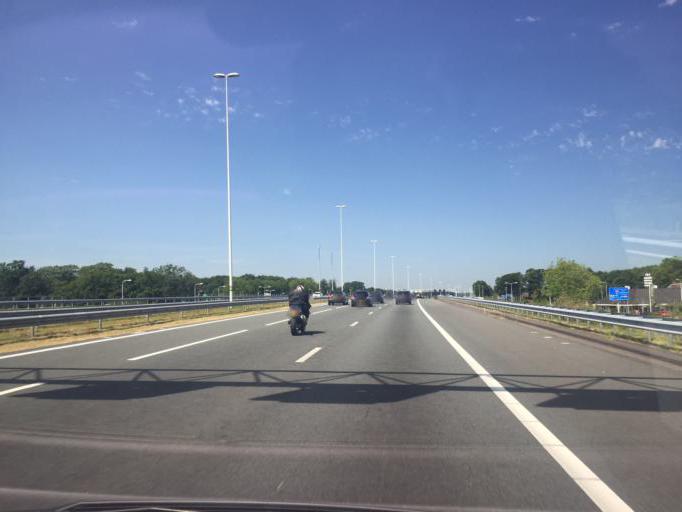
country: NL
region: Utrecht
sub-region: Gemeente Utrechtse Heuvelrug
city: Maarsbergen
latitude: 52.0542
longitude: 5.4059
